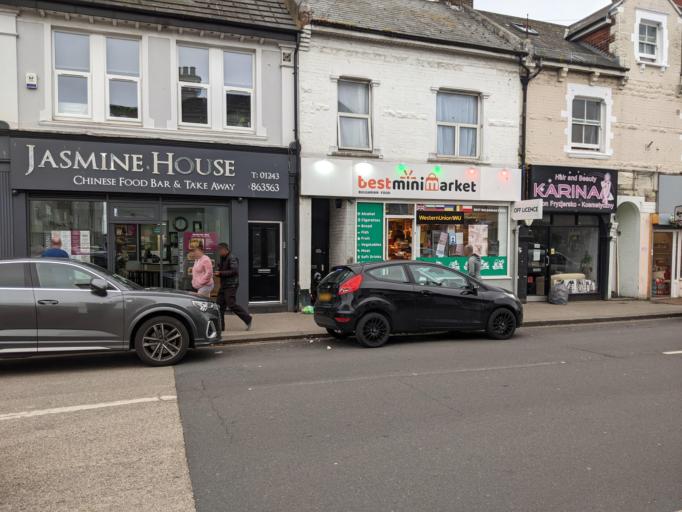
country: GB
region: England
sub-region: West Sussex
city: Bognor Regis
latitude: 50.7861
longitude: -0.6760
